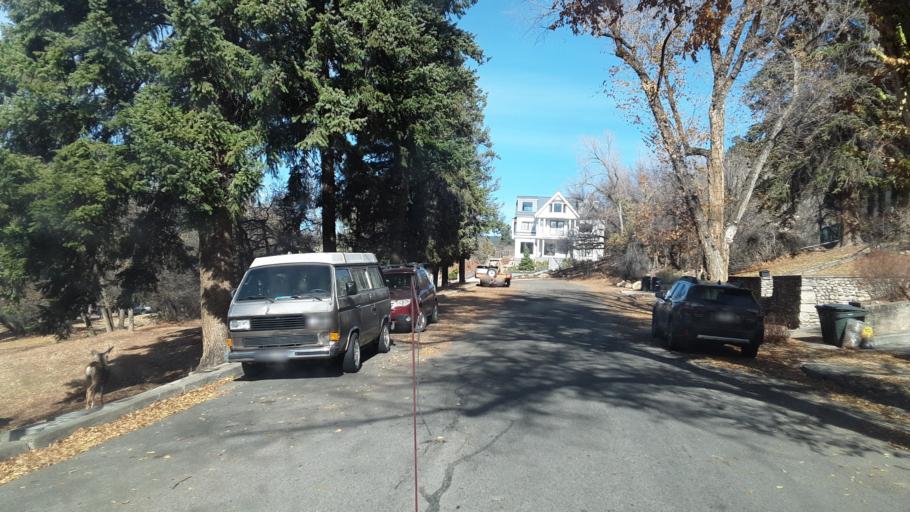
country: US
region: Colorado
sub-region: La Plata County
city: Durango
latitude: 37.2761
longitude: -107.8753
